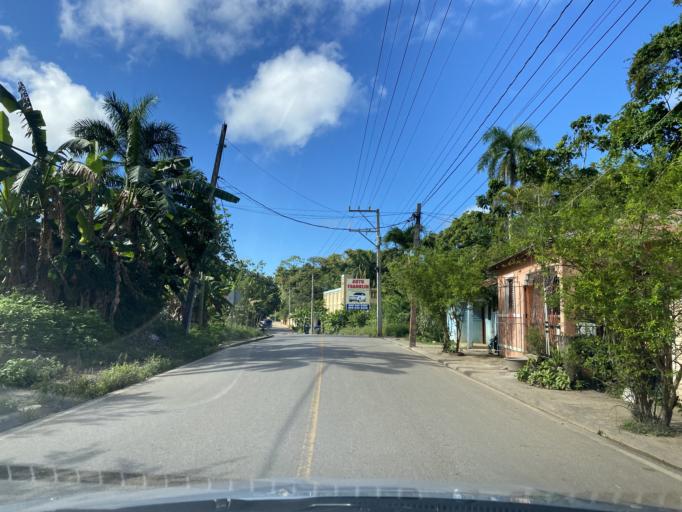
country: DO
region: Samana
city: Las Terrenas
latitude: 19.2937
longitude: -69.5477
